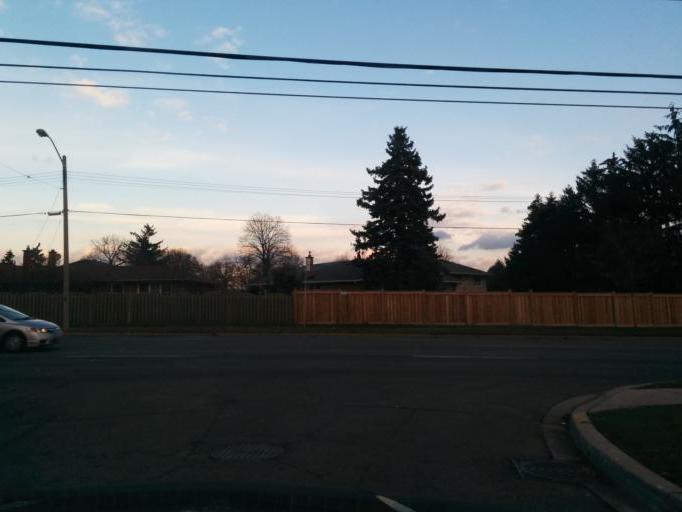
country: CA
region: Ontario
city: Etobicoke
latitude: 43.6846
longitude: -79.5414
